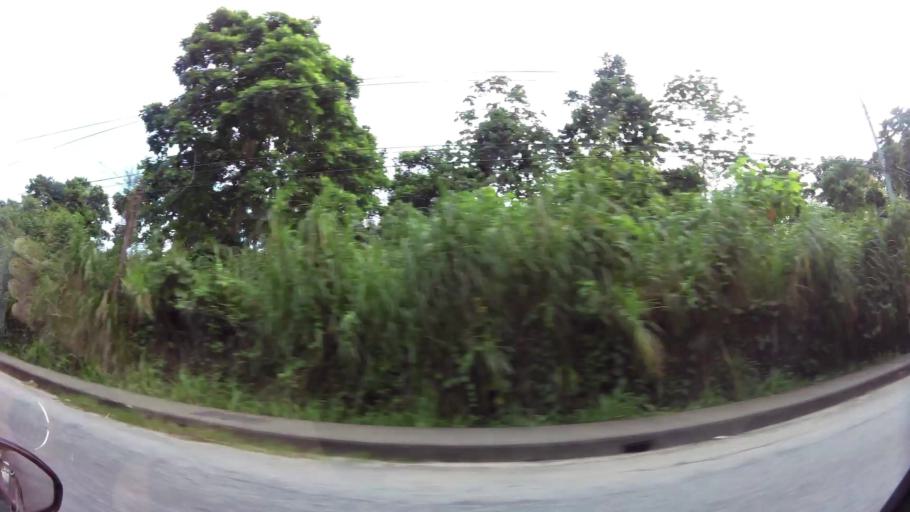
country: TT
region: San Juan/Laventille
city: Laventille
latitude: 10.7092
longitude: -61.4634
